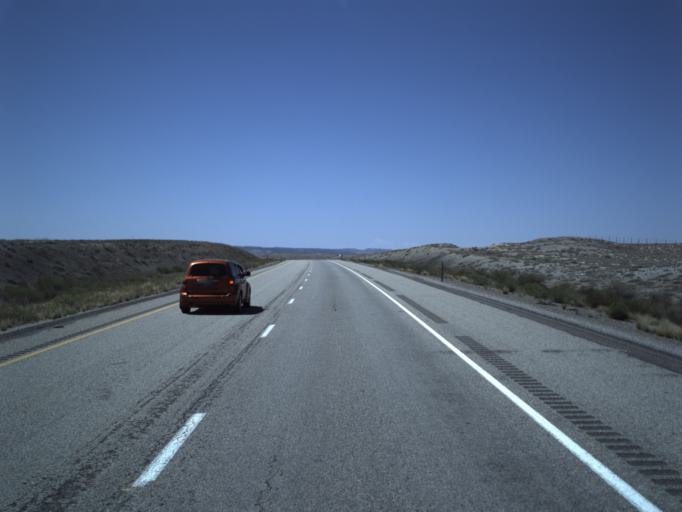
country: US
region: Utah
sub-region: Grand County
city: Moab
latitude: 38.9947
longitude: -109.3297
